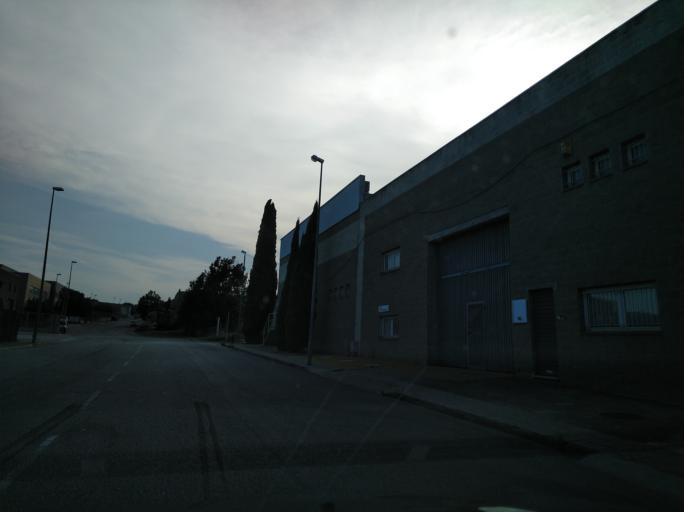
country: ES
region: Catalonia
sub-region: Provincia de Girona
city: Vilablareix
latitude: 41.9447
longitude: 2.7829
